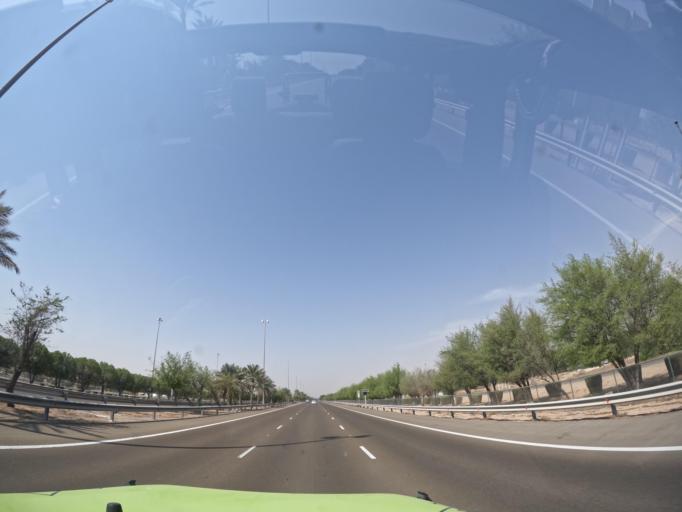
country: AE
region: Abu Dhabi
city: Al Ain
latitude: 24.1796
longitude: 55.3187
